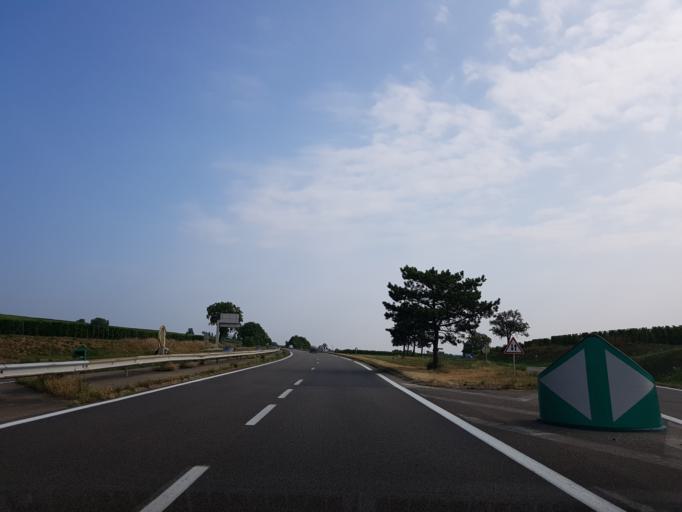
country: FR
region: Alsace
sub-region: Departement du Haut-Rhin
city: Herrlisheim-pres-Colmar
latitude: 48.0132
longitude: 7.3079
